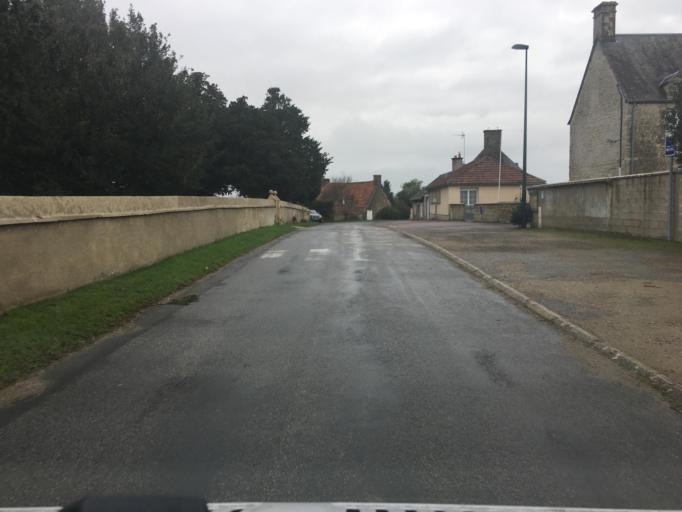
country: FR
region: Lower Normandy
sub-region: Departement de la Manche
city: Sainte-Mere-Eglise
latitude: 49.4369
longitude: -1.2591
